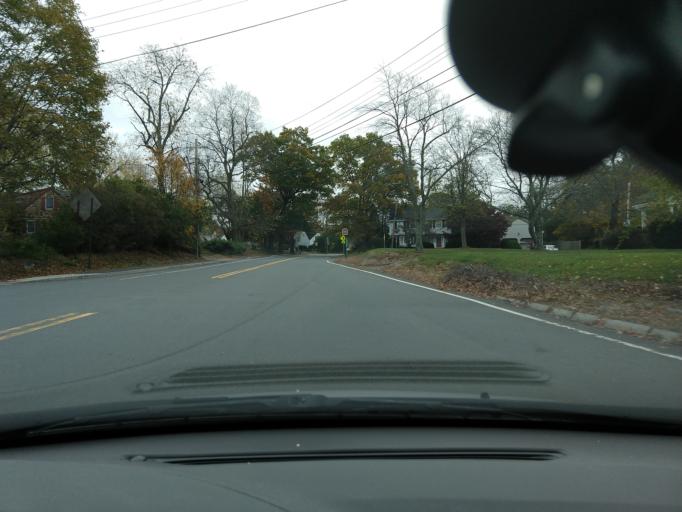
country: US
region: Massachusetts
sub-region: Middlesex County
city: Lexington
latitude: 42.4421
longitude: -71.2541
